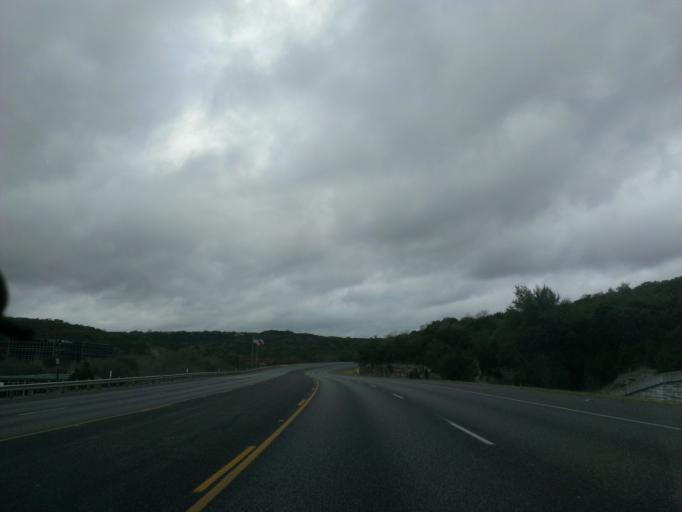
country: US
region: Texas
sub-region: Williamson County
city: Jollyville
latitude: 30.3825
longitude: -97.8136
